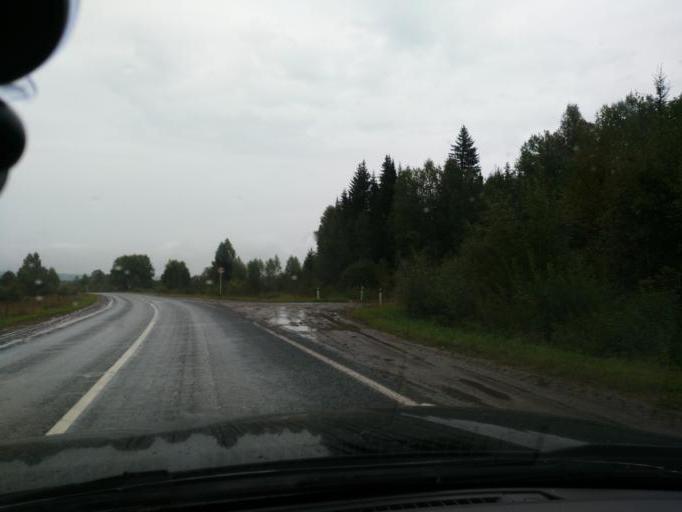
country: RU
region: Perm
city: Yugo-Kamskiy
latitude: 57.5313
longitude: 55.6886
